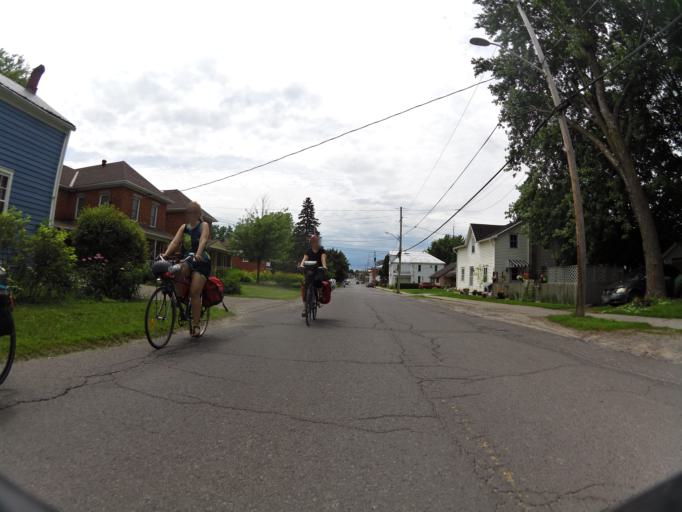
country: CA
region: Ontario
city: Prescott
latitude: 45.0194
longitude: -75.6445
